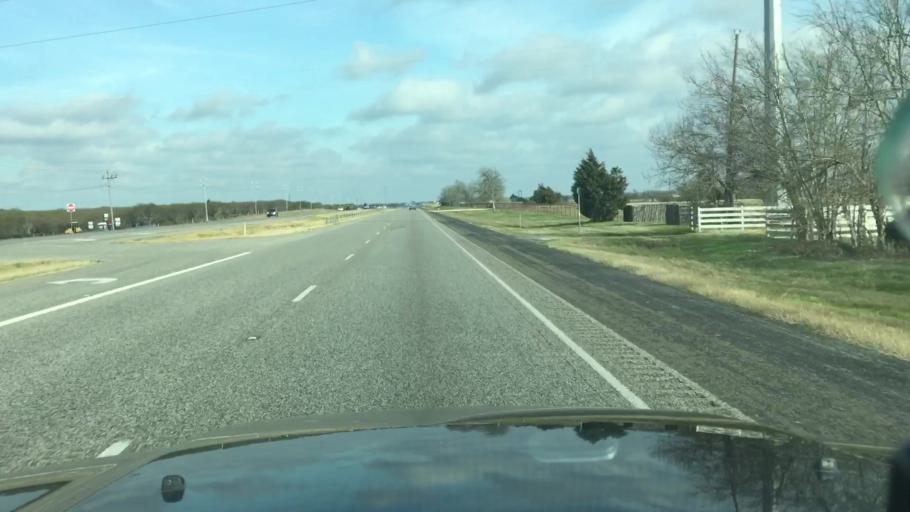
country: US
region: Texas
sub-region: Washington County
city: Brenham
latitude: 30.1374
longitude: -96.3261
